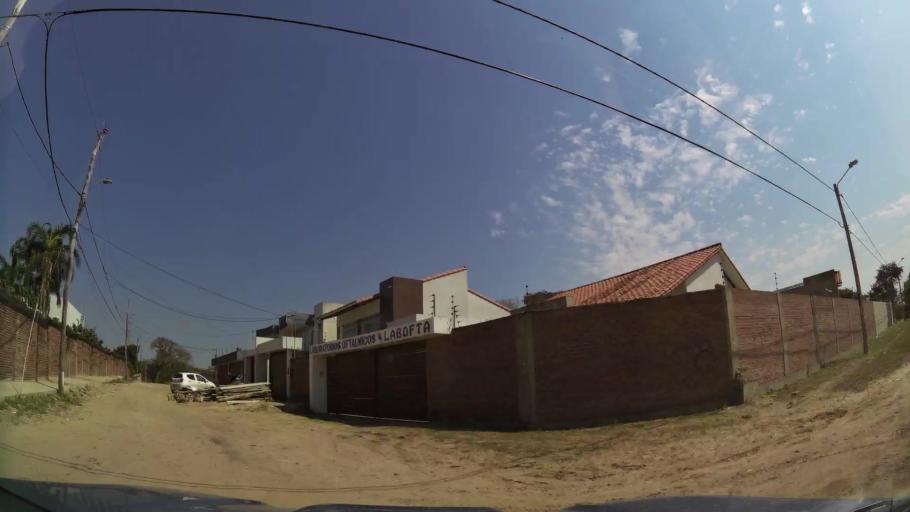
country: BO
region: Santa Cruz
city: Santa Cruz de la Sierra
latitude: -17.7480
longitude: -63.1946
